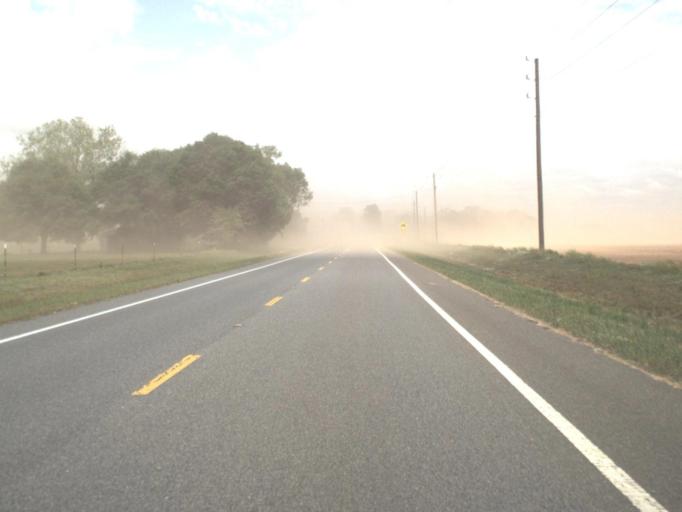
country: US
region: Florida
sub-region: Santa Rosa County
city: Point Baker
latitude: 30.8065
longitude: -87.1033
